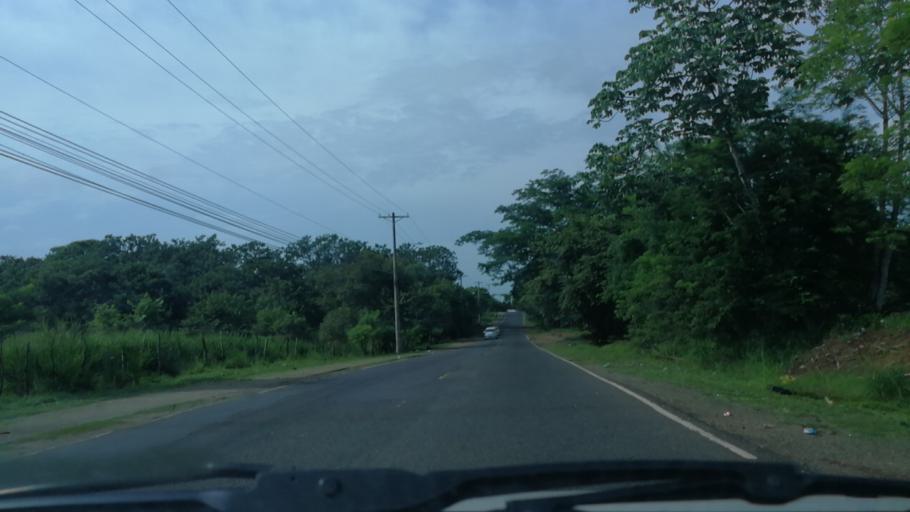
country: PA
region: Panama
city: Pacora
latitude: 9.0945
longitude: -79.2885
